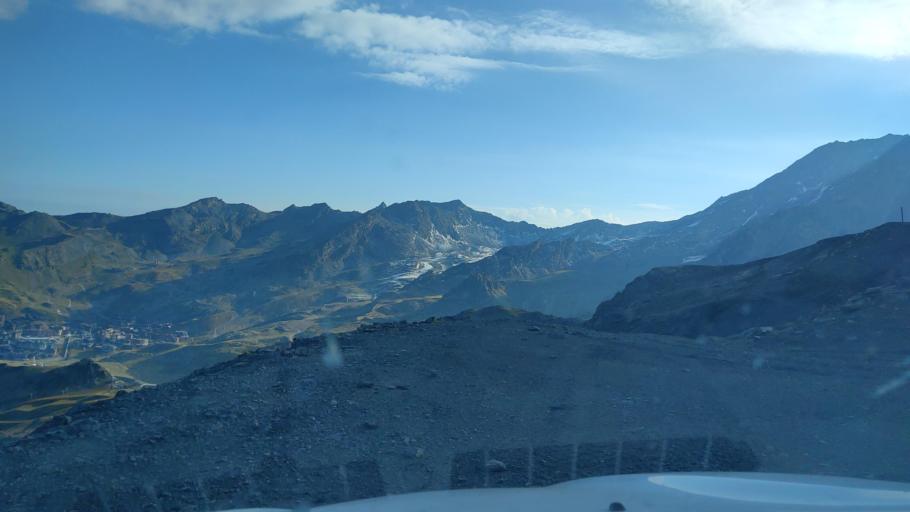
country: FR
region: Rhone-Alpes
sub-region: Departement de la Savoie
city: Val Thorens
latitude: 45.2690
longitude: 6.5777
